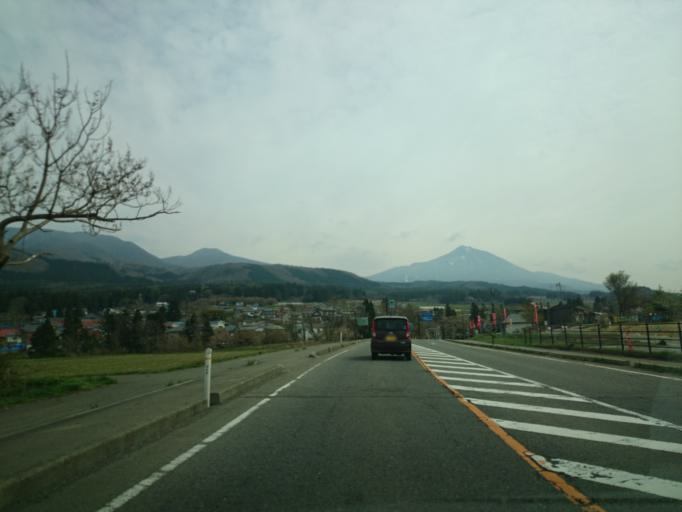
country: JP
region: Fukushima
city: Inawashiro
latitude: 37.5633
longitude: 139.9865
